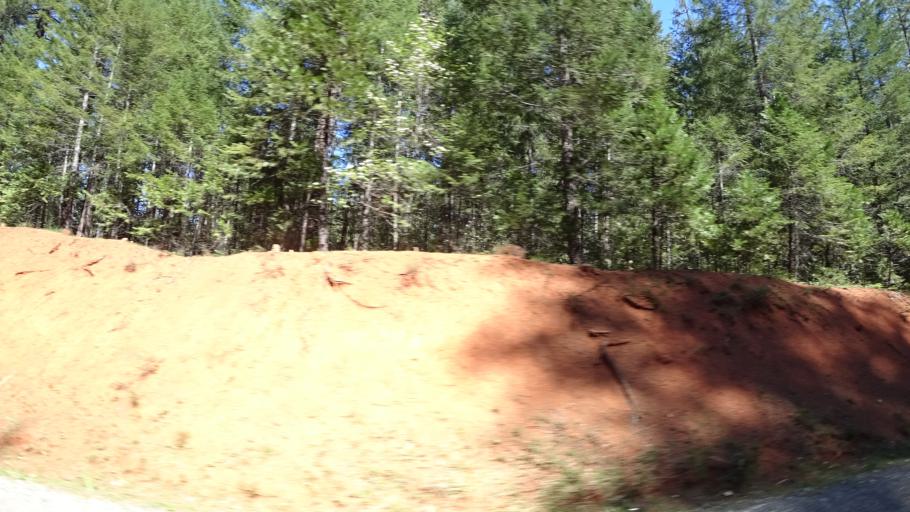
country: US
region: California
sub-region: Trinity County
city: Lewiston
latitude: 40.8858
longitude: -122.7960
